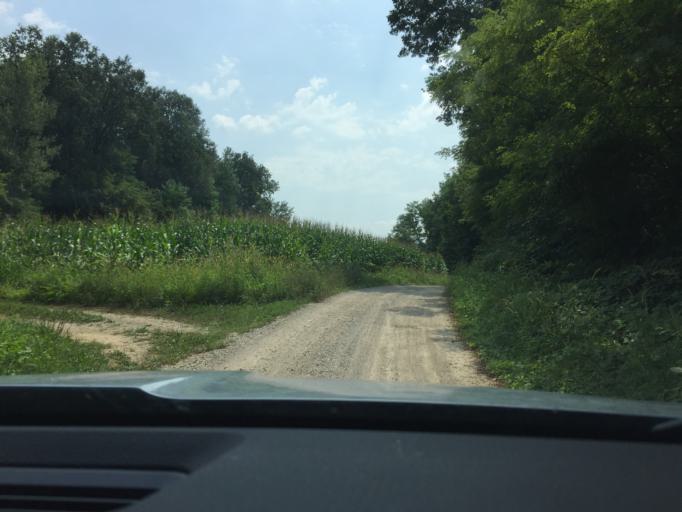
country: SI
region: Metlika
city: Metlika
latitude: 45.6531
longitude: 15.3464
